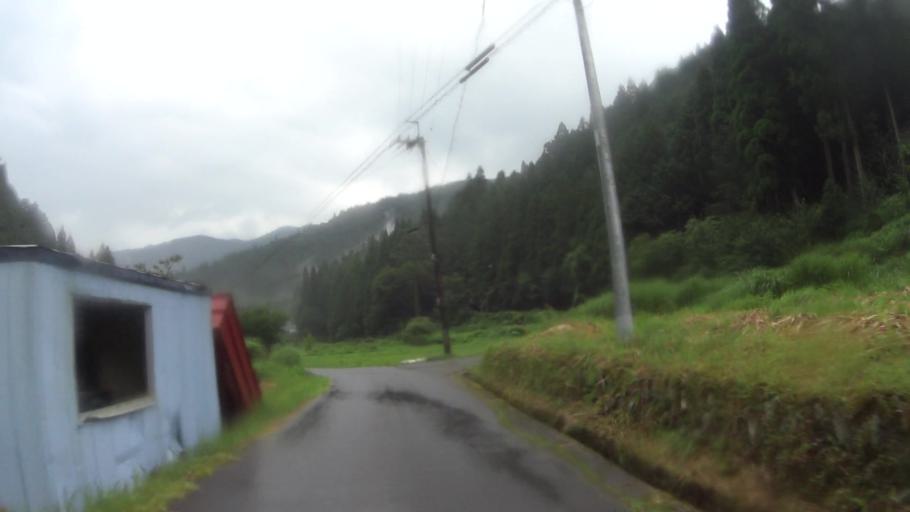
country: JP
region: Shiga Prefecture
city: Kitahama
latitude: 35.2643
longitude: 135.8144
